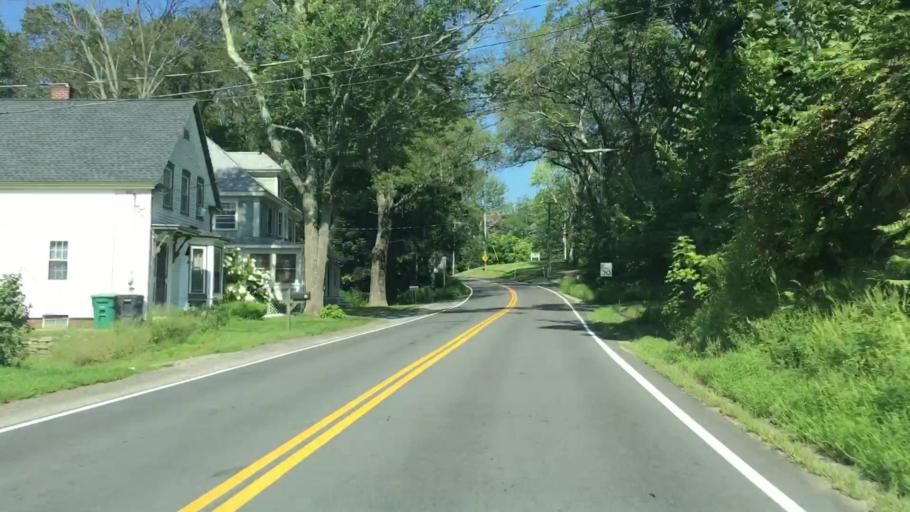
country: US
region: New Hampshire
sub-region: Rockingham County
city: East Kingston
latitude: 42.9238
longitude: -71.0106
